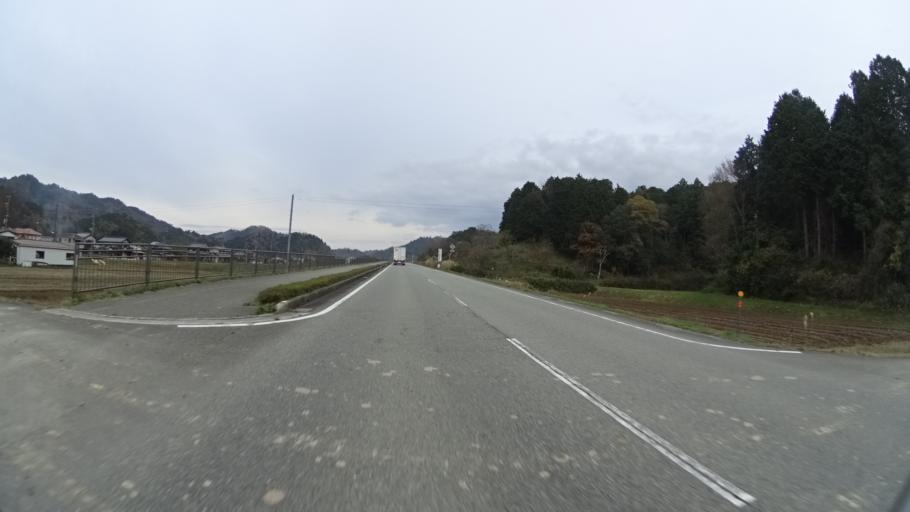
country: JP
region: Hyogo
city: Sasayama
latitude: 35.0685
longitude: 135.2998
